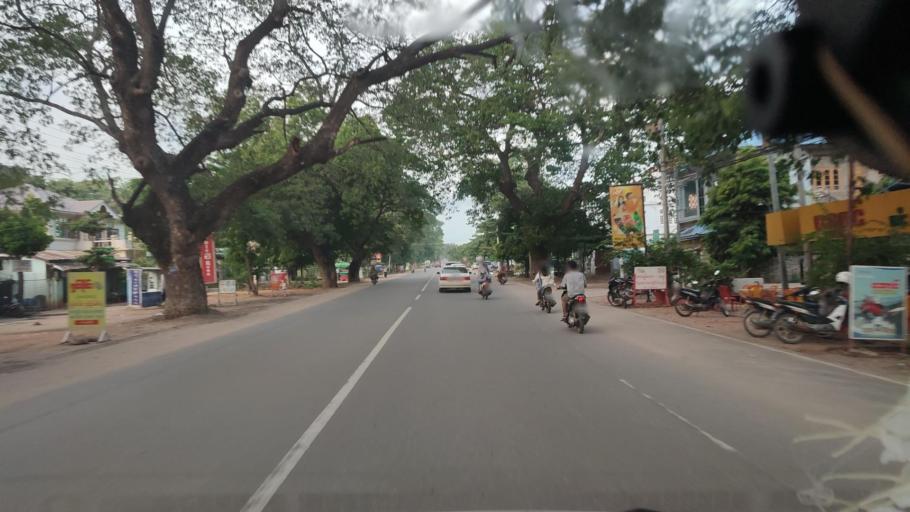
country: MM
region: Magway
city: Magway
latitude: 20.1405
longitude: 94.9401
